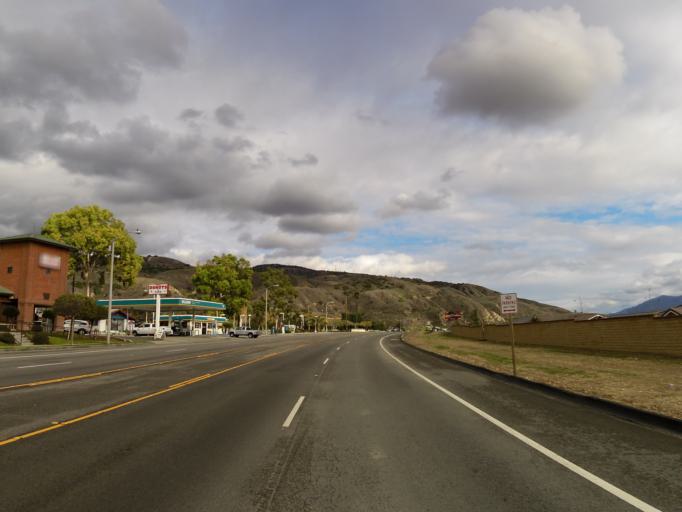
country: US
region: California
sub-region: Ventura County
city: Fillmore
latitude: 34.3987
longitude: -118.9057
